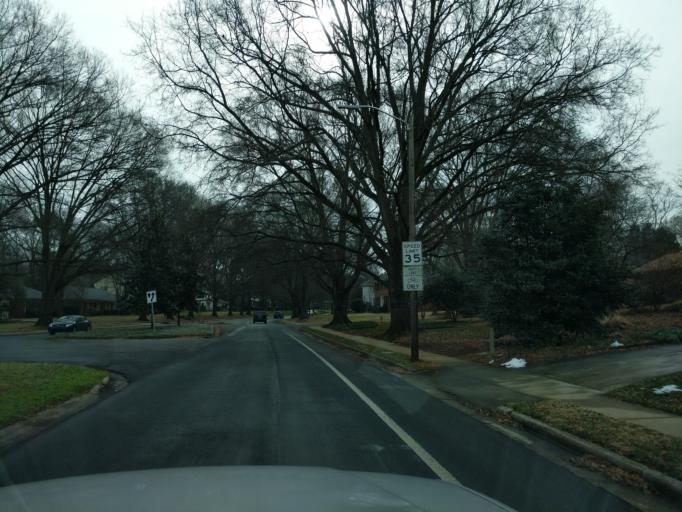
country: US
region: North Carolina
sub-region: Mecklenburg County
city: Charlotte
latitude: 35.1636
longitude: -80.8287
